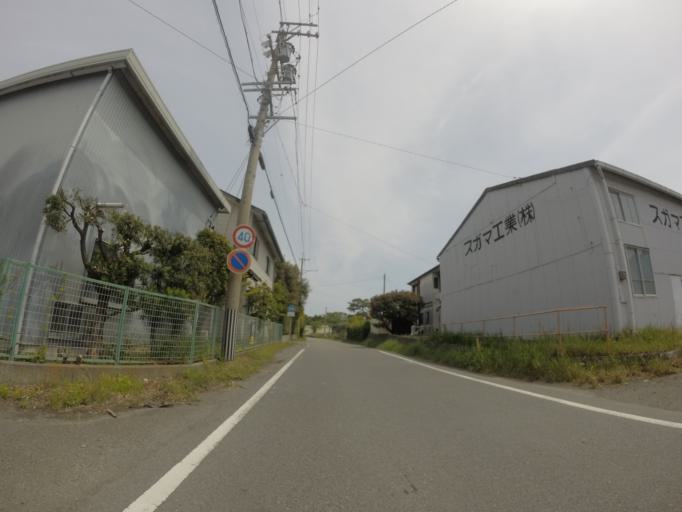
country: JP
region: Shizuoka
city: Yaizu
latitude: 34.8042
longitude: 138.3159
